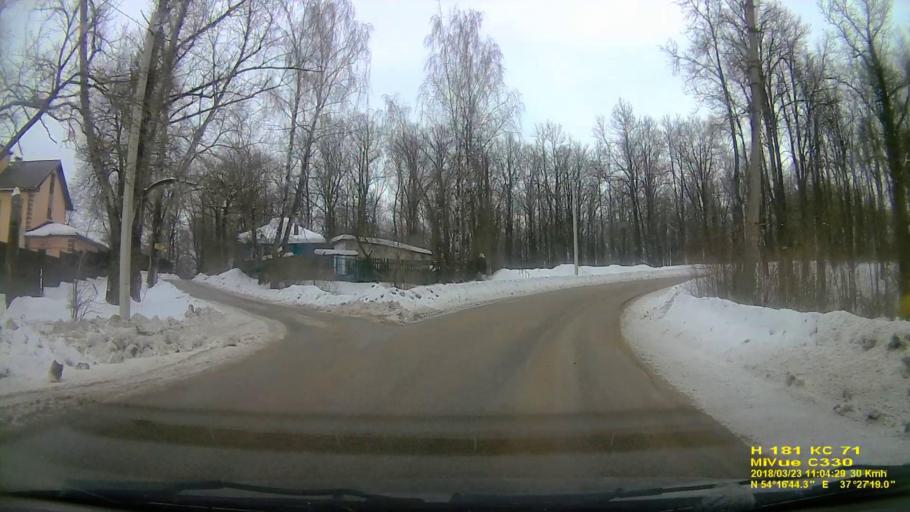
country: RU
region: Tula
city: Leninskiy
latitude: 54.2790
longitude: 37.4553
